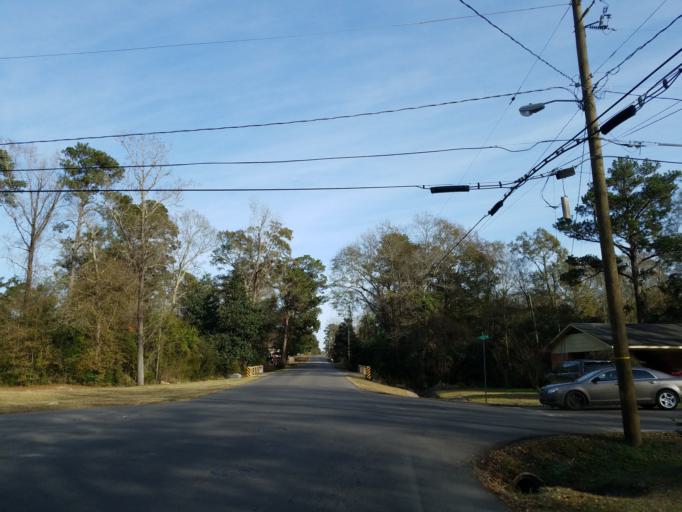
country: US
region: Mississippi
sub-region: Forrest County
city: Hattiesburg
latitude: 31.3174
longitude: -89.3144
